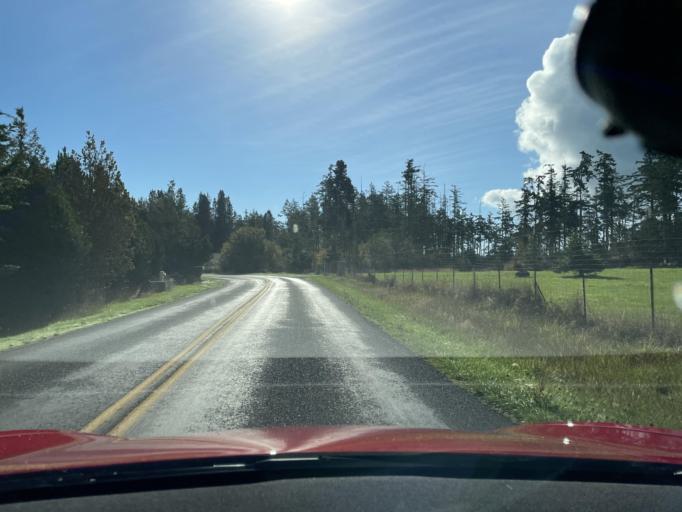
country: US
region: Washington
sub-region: San Juan County
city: Friday Harbor
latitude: 48.5066
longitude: -123.0210
